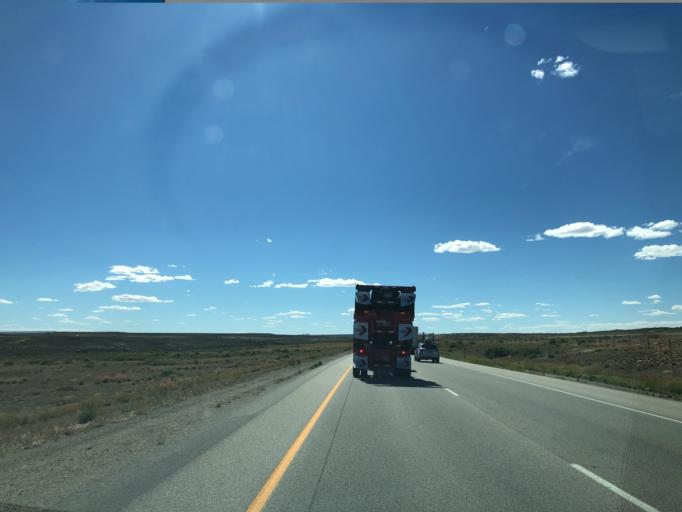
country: US
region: Wyoming
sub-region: Carbon County
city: Rawlins
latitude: 41.7051
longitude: -107.8387
